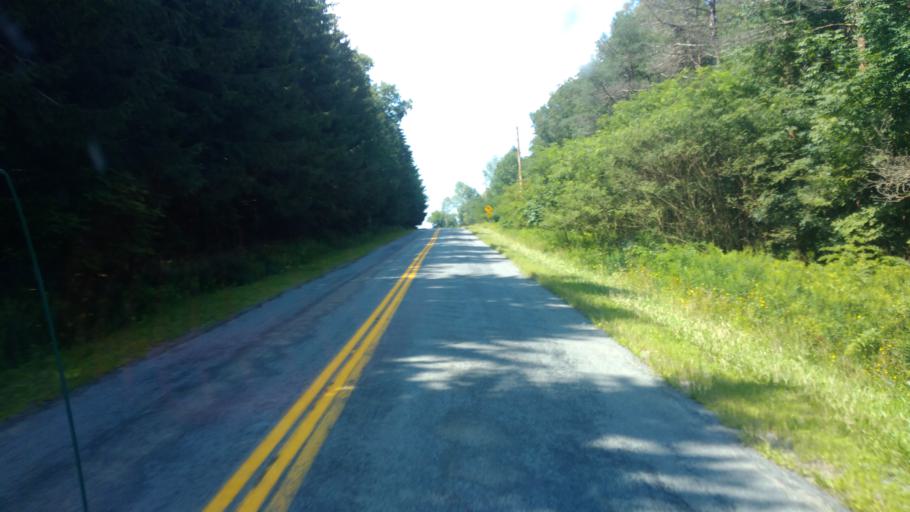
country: US
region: New York
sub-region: Steuben County
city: Canisteo
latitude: 42.3524
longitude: -77.5528
